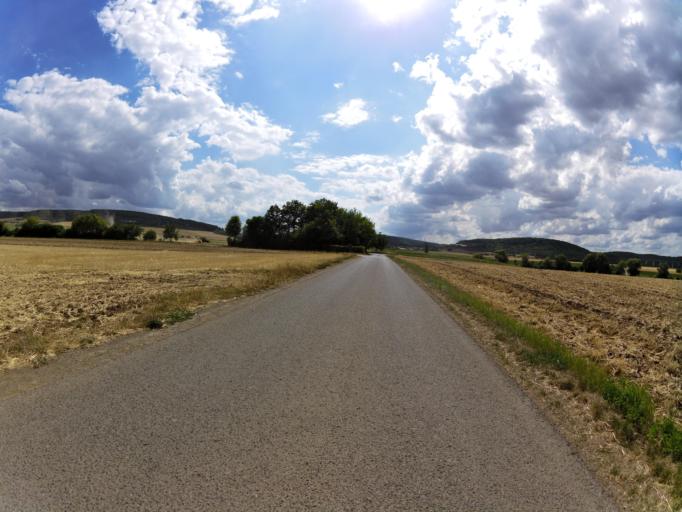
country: DE
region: Bavaria
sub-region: Regierungsbezirk Unterfranken
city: Zellingen
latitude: 49.8861
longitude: 9.8113
